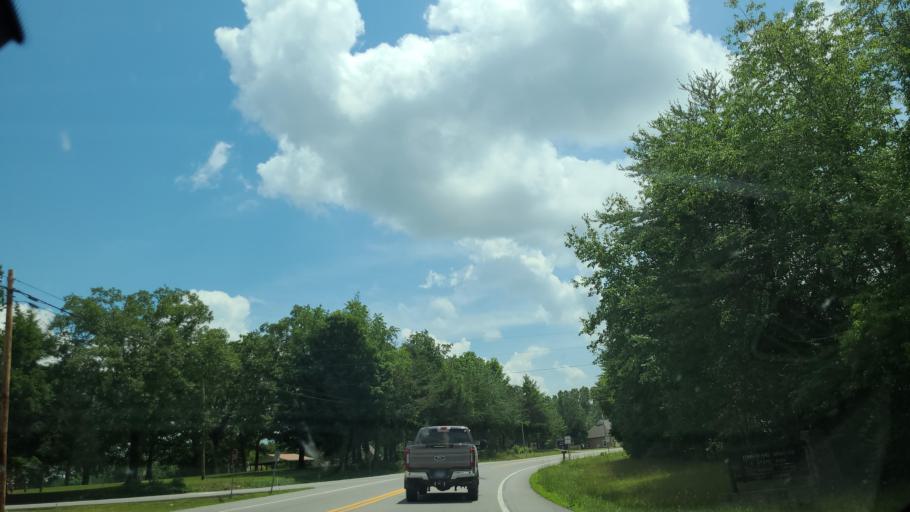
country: US
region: Tennessee
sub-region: Cumberland County
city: Crossville
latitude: 35.9049
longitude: -84.9856
